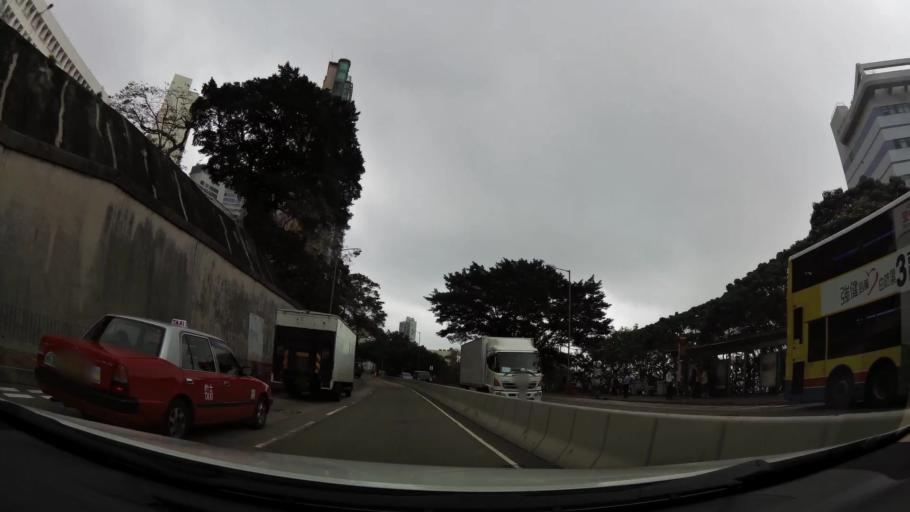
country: HK
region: Central and Western
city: Central
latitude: 22.2691
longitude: 114.1308
